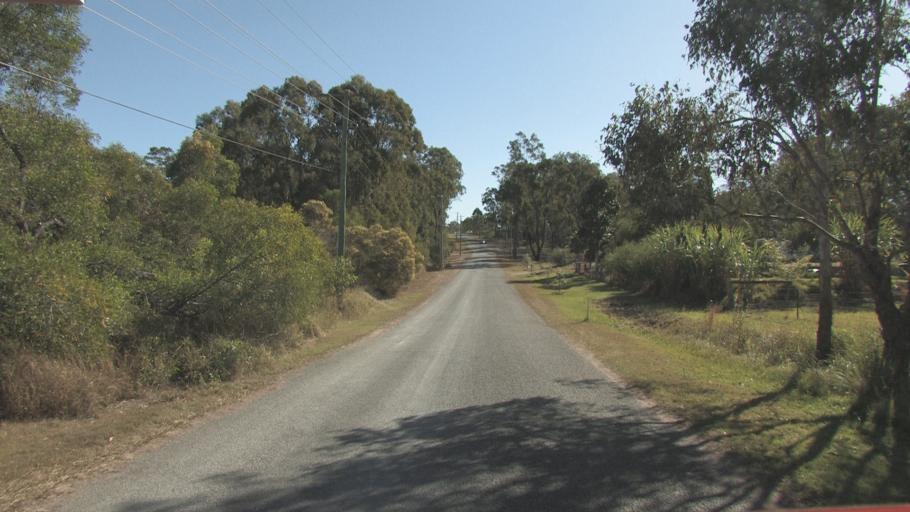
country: AU
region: Queensland
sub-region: Logan
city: Cedar Vale
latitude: -27.8562
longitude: 153.0168
